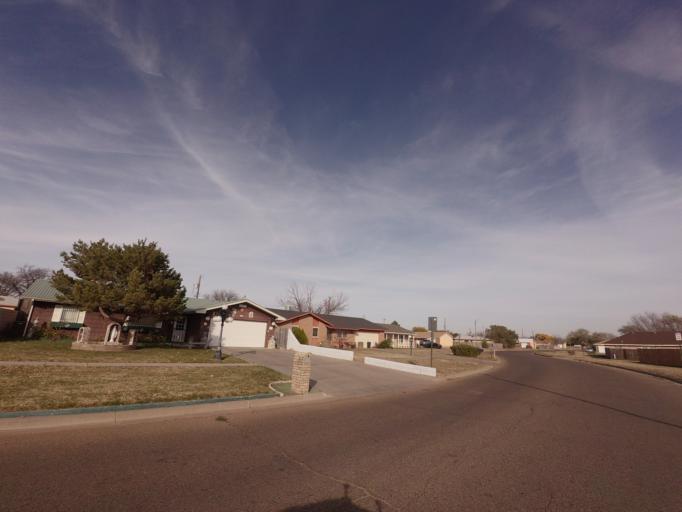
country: US
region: New Mexico
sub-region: Curry County
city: Clovis
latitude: 34.4275
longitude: -103.2299
